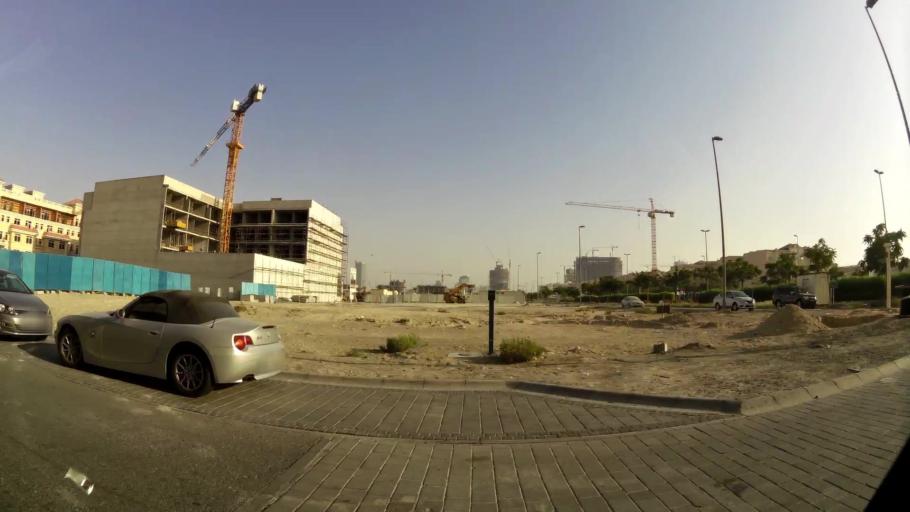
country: AE
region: Dubai
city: Dubai
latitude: 25.0657
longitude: 55.2103
